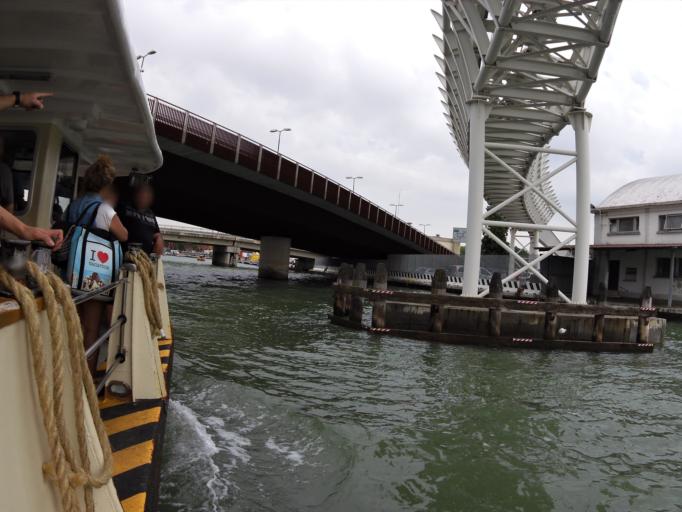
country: IT
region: Veneto
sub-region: Provincia di Venezia
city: Venice
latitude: 45.4412
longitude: 12.3096
